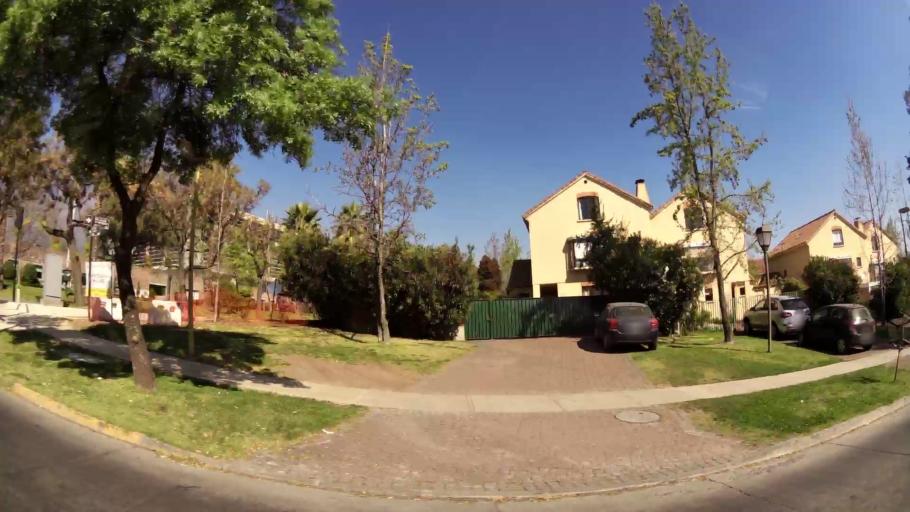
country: CL
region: Santiago Metropolitan
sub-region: Provincia de Santiago
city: Villa Presidente Frei, Nunoa, Santiago, Chile
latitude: -33.3998
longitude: -70.5105
